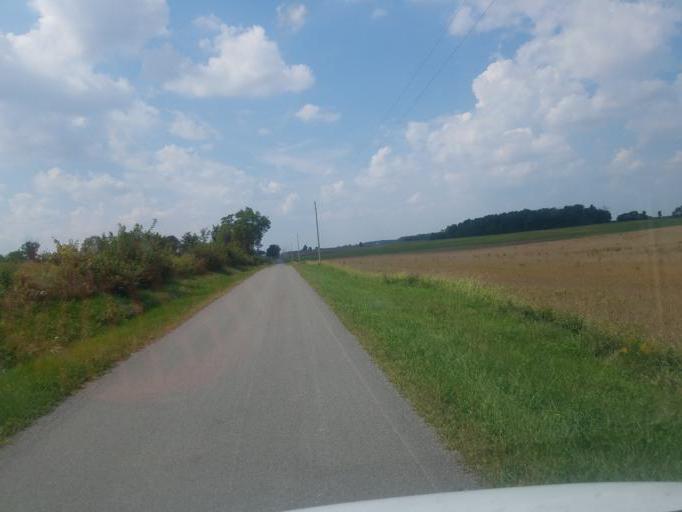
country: US
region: Ohio
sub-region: Hardin County
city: Ada
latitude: 40.6377
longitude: -83.8574
